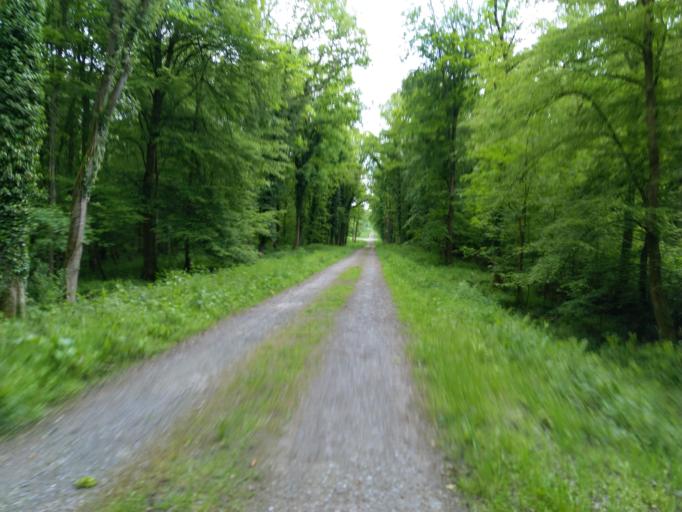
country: FR
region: Nord-Pas-de-Calais
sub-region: Departement du Nord
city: Gommegnies
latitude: 50.2238
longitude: 3.7077
